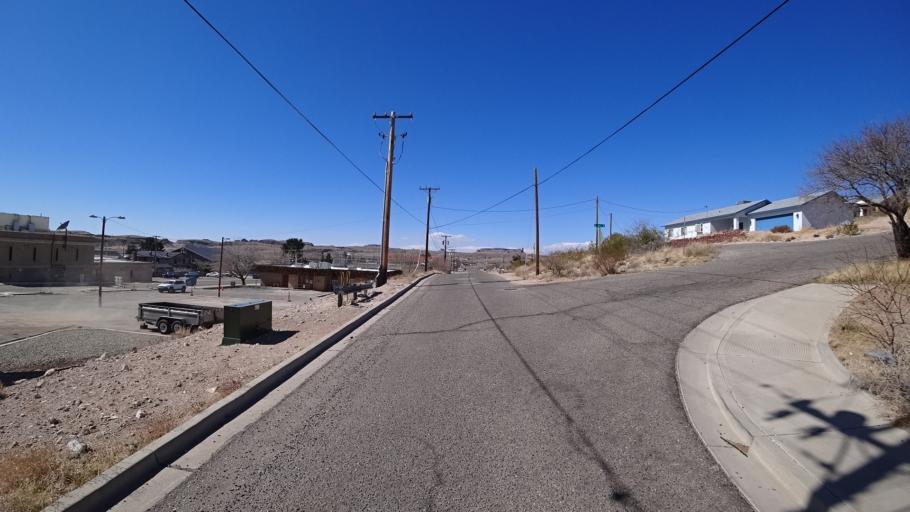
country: US
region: Arizona
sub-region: Mohave County
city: Kingman
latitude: 35.1928
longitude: -114.0524
